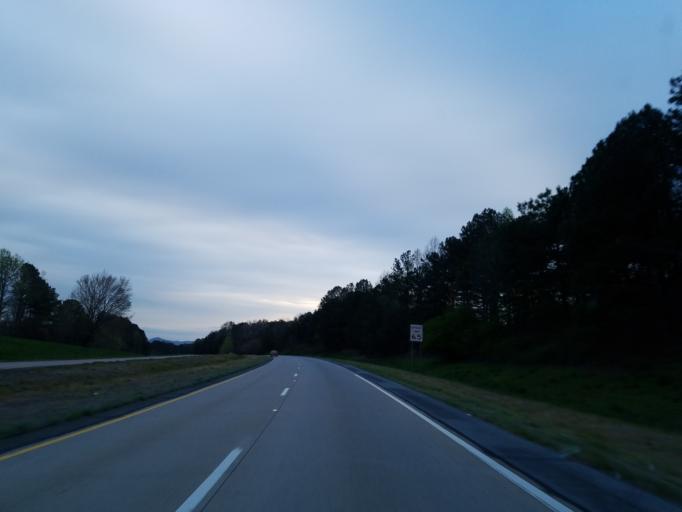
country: US
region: Georgia
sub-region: Gilmer County
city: Ellijay
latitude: 34.5770
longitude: -84.5209
